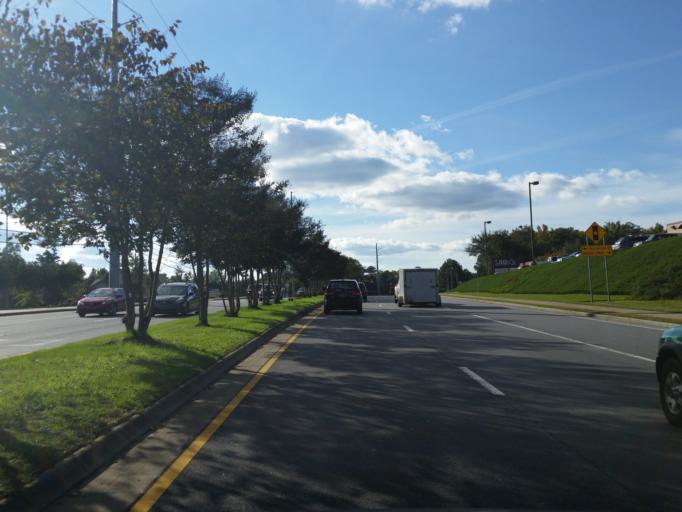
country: US
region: Georgia
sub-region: Cobb County
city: Kennesaw
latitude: 33.9465
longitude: -84.6278
